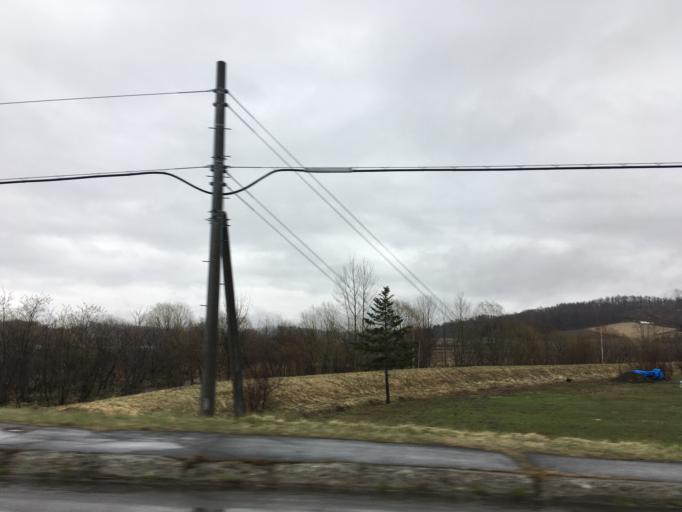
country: JP
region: Hokkaido
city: Nayoro
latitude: 44.1128
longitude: 142.4796
